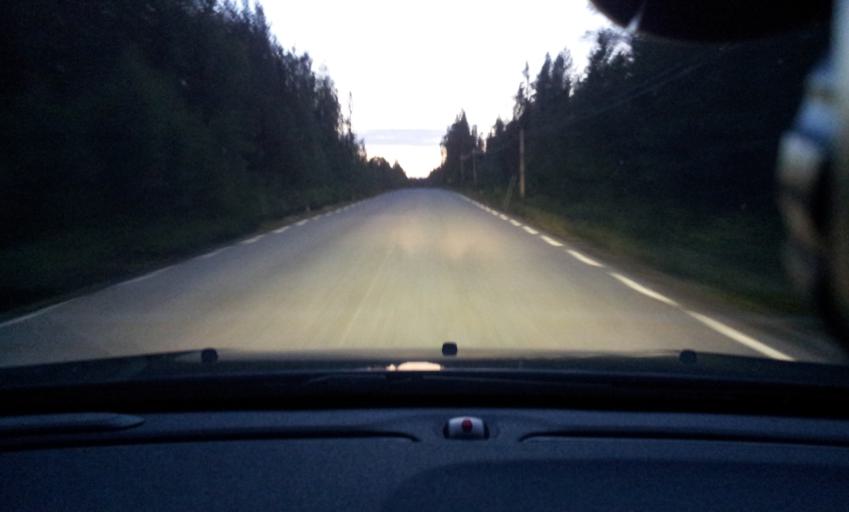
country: SE
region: Jaemtland
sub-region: Bergs Kommun
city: Hoverberg
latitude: 62.7433
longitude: 14.5821
